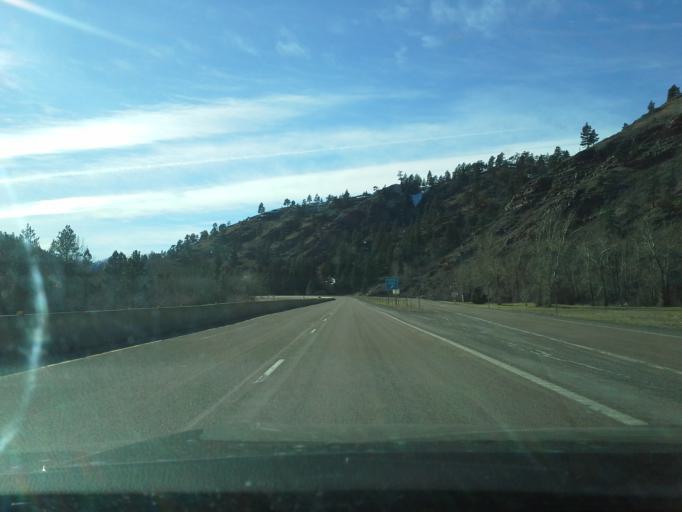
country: US
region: Montana
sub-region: Lewis and Clark County
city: Helena Valley Northwest
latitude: 46.9552
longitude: -112.1043
